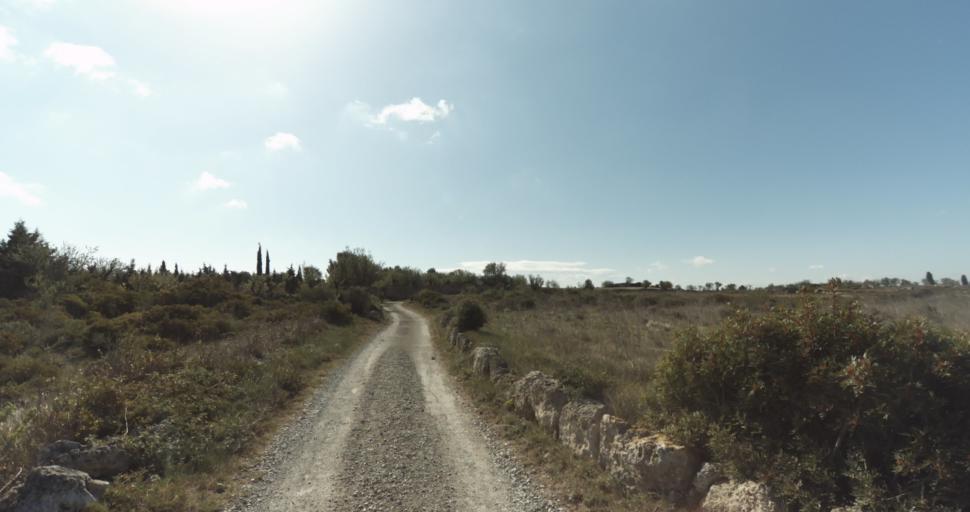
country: FR
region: Languedoc-Roussillon
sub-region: Departement de l'Aude
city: Leucate
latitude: 42.9252
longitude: 3.0312
